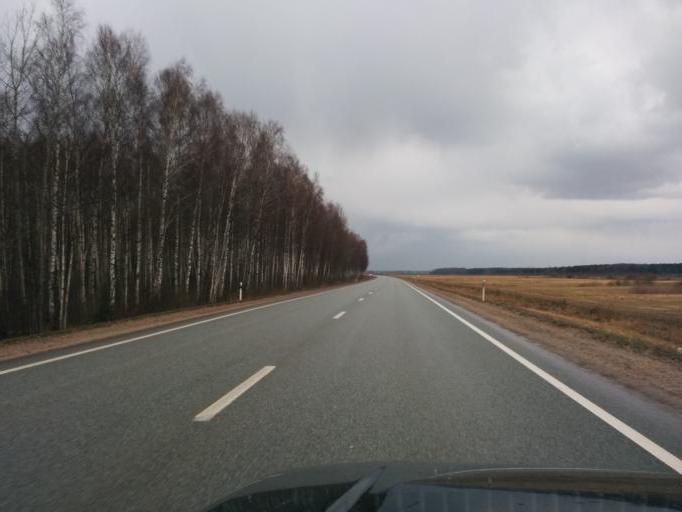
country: LV
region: Marupe
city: Marupe
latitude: 56.8516
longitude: 24.0056
